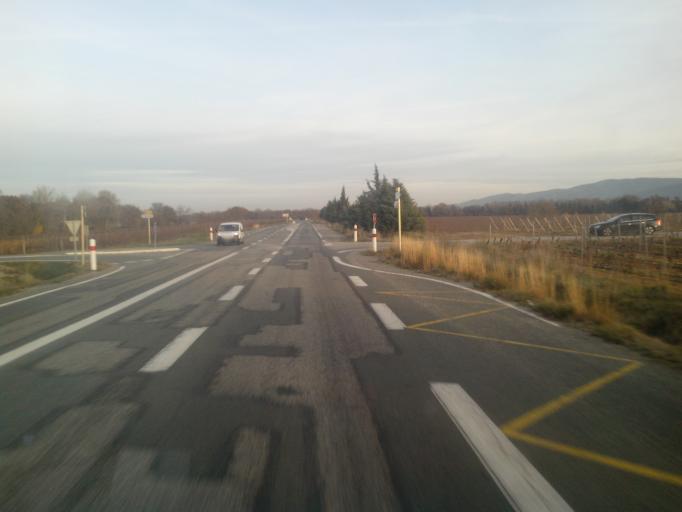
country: FR
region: Languedoc-Roussillon
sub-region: Departement de l'Aude
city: Trebes
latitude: 43.1991
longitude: 2.4962
